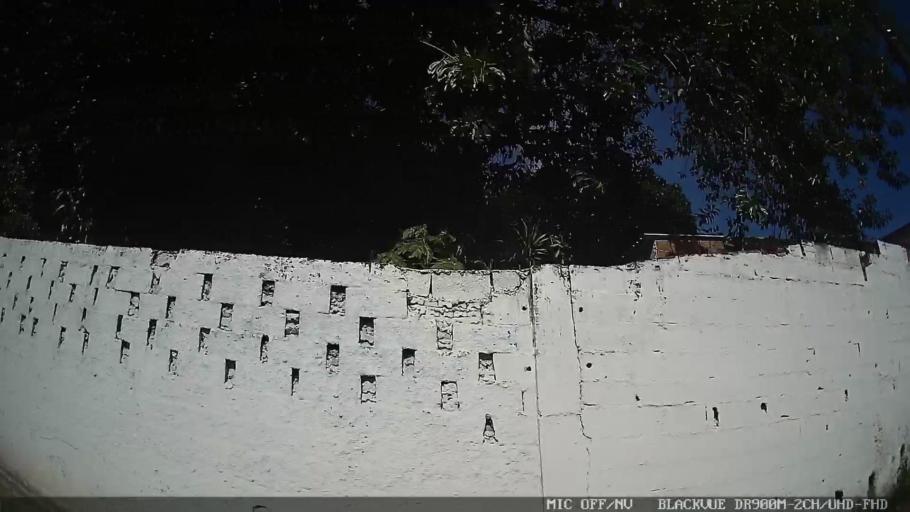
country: BR
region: Sao Paulo
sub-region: Guaruja
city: Guaruja
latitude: -23.9913
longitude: -46.2685
